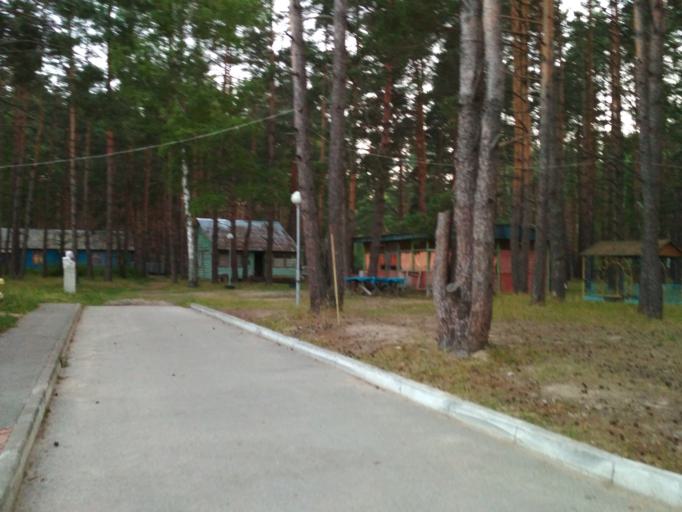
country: RU
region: Rjazan
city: Solotcha
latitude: 54.8289
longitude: 39.9388
